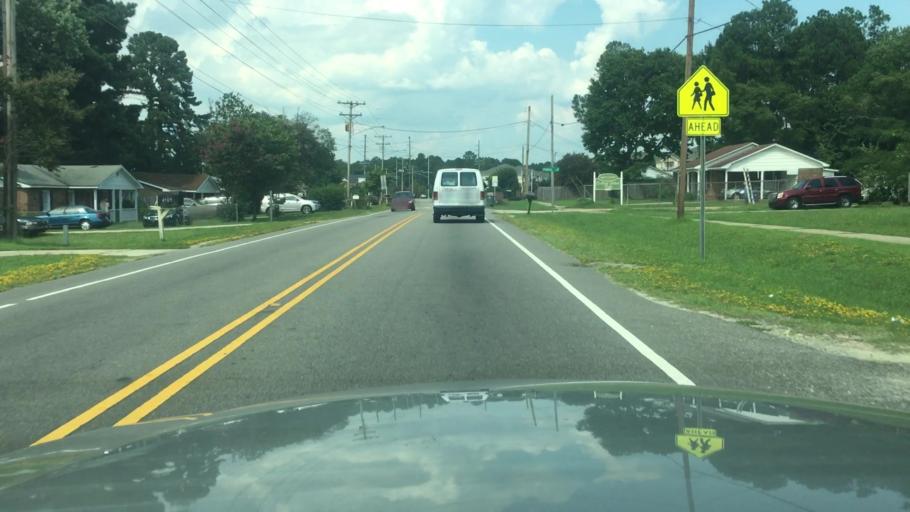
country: US
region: North Carolina
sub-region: Cumberland County
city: Fayetteville
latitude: 35.1245
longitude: -78.9007
